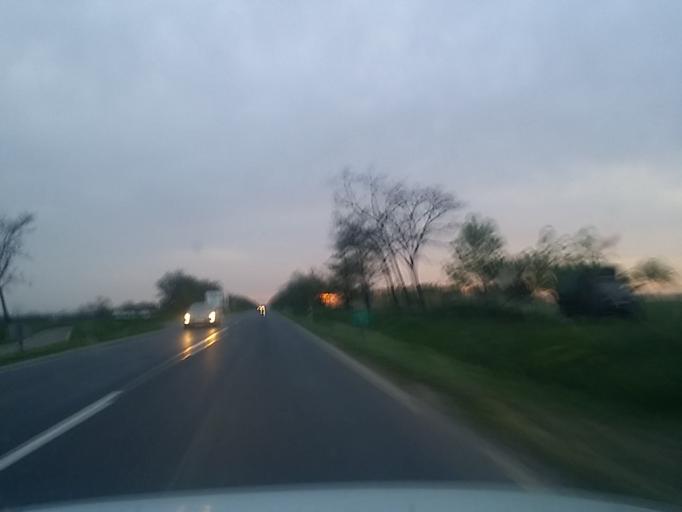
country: HU
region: Bekes
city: Mezobereny
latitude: 46.7104
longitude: 20.9738
